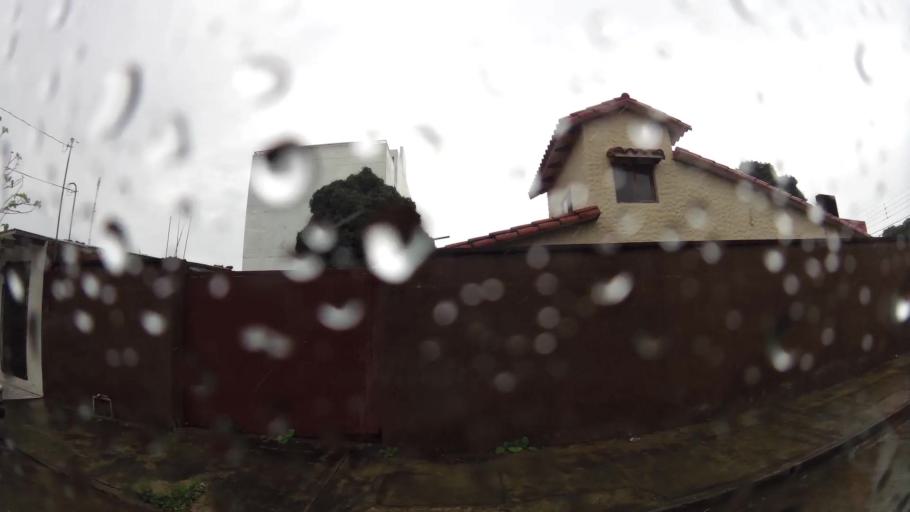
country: BO
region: Santa Cruz
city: Santa Cruz de la Sierra
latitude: -17.7797
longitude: -63.1954
